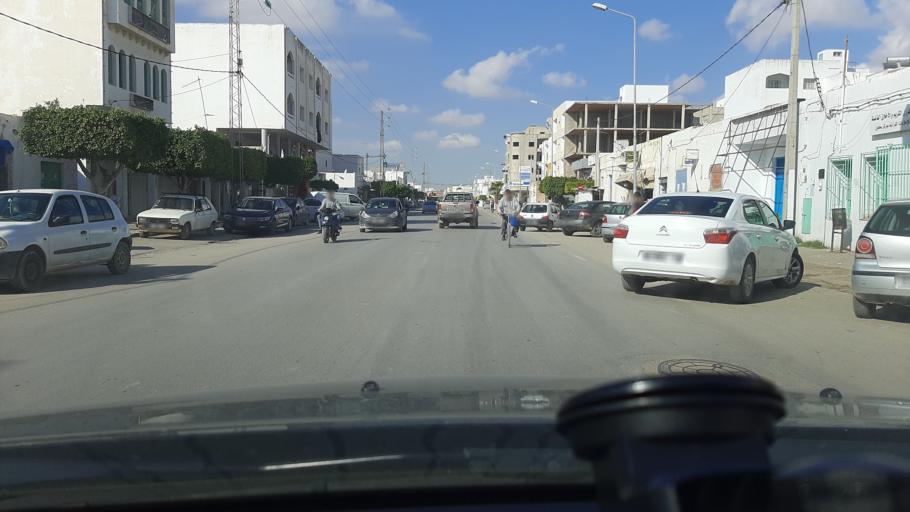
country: TN
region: Safaqis
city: Sfax
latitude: 34.7942
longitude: 10.7147
